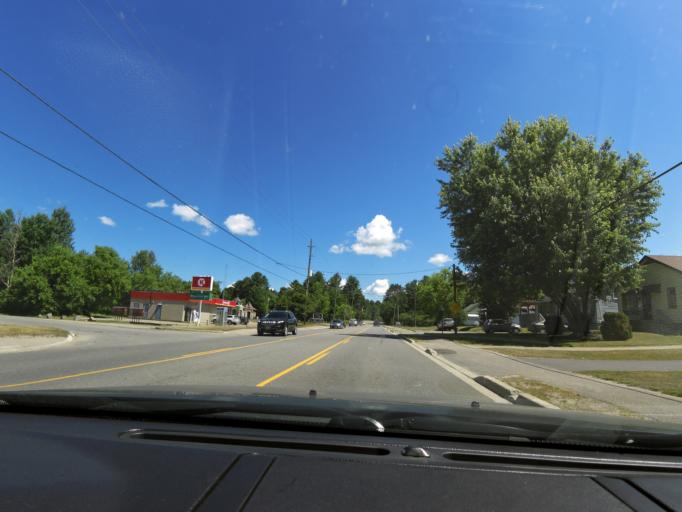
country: CA
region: Ontario
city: Bracebridge
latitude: 45.0456
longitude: -79.3011
